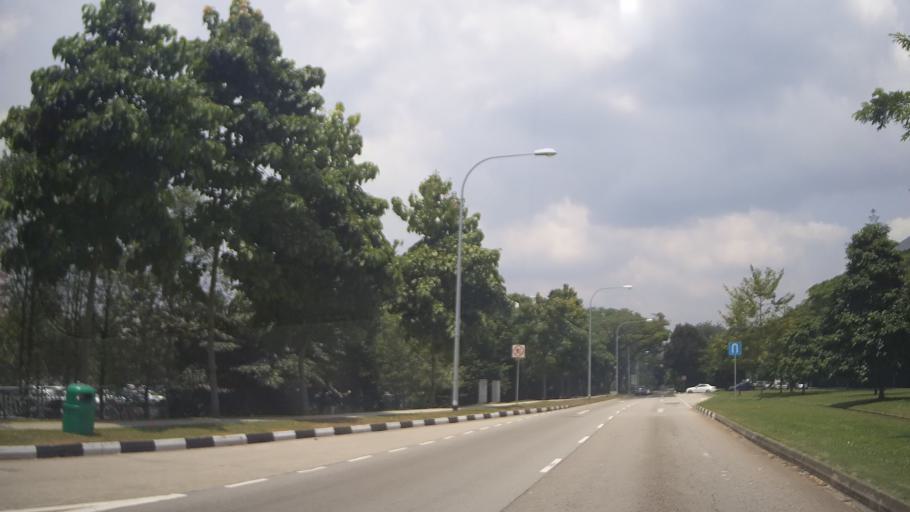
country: MY
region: Johor
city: Johor Bahru
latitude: 1.4544
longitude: 103.7957
